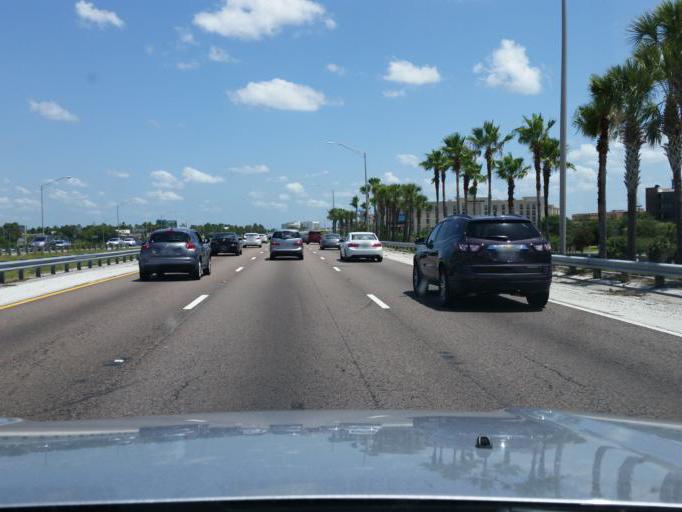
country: US
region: Florida
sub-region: Orange County
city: Doctor Phillips
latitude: 28.4502
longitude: -81.4742
